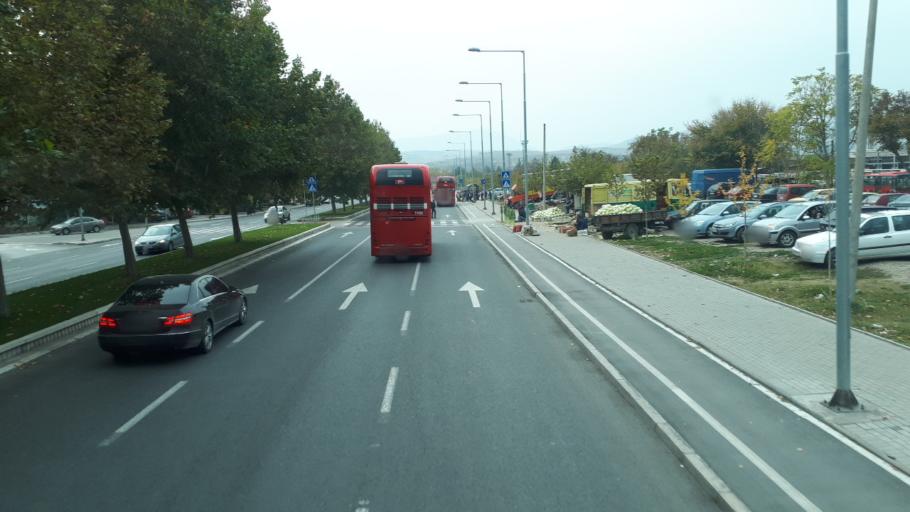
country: MK
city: Krushopek
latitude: 42.0093
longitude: 21.3663
